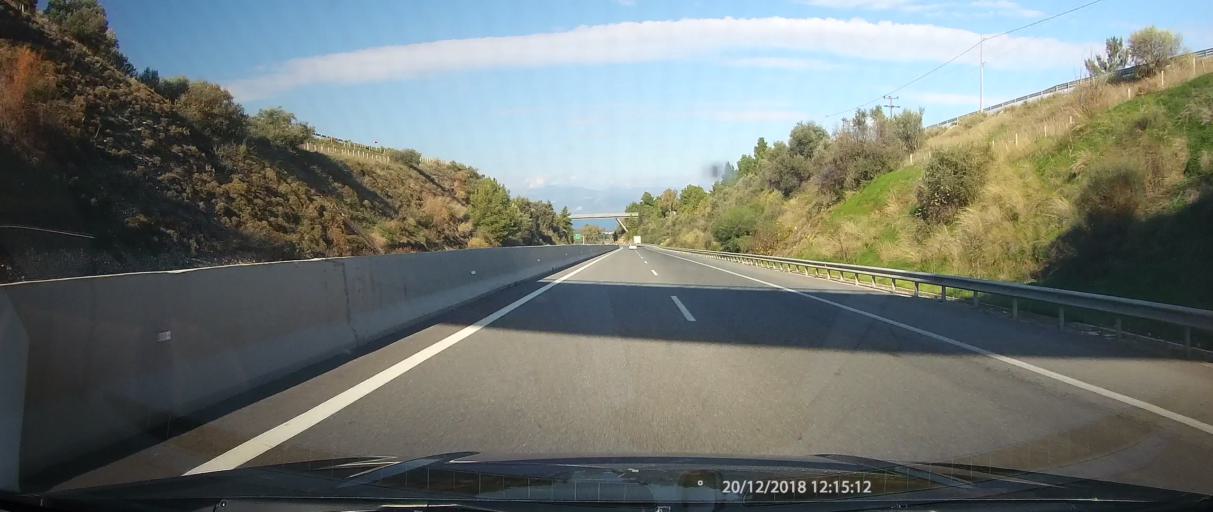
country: GR
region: West Greece
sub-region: Nomos Achaias
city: Aigio
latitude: 38.2491
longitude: 22.0712
